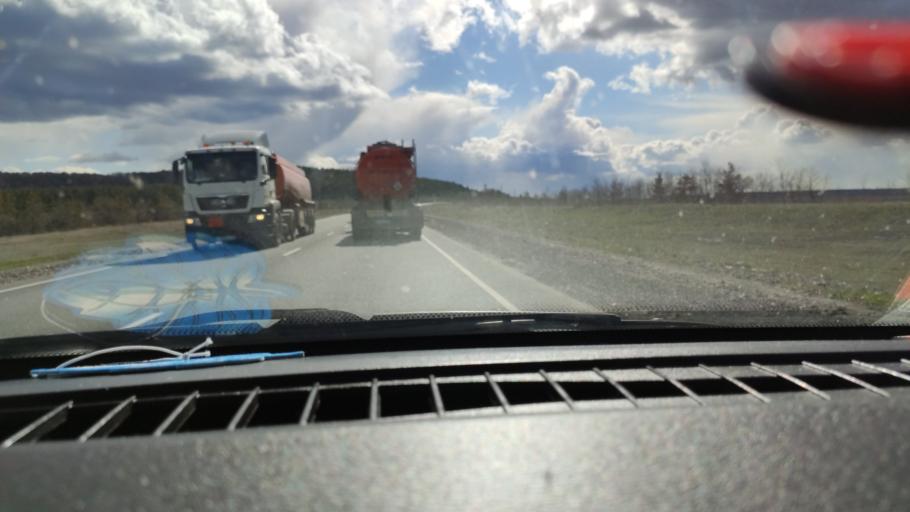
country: RU
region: Saratov
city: Khvalynsk
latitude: 52.5439
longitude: 48.0638
